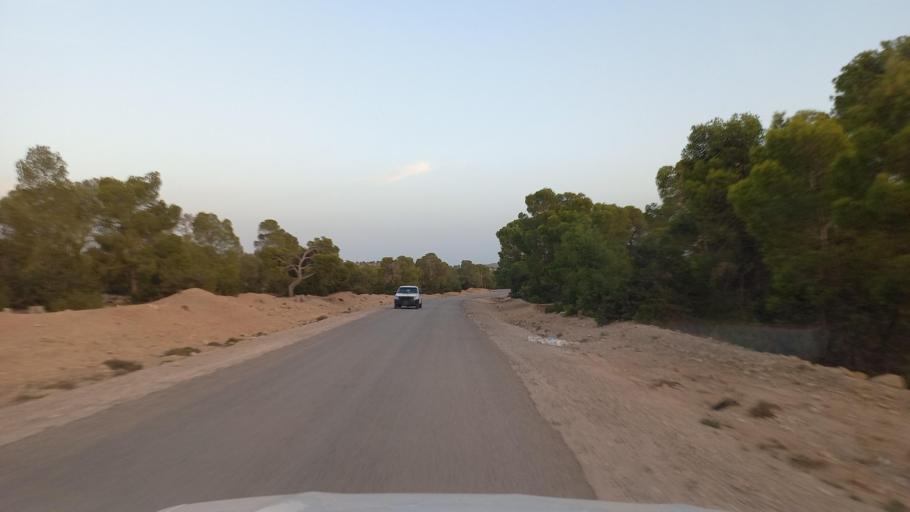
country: TN
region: Al Qasrayn
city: Sbiba
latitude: 35.4125
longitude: 8.9433
